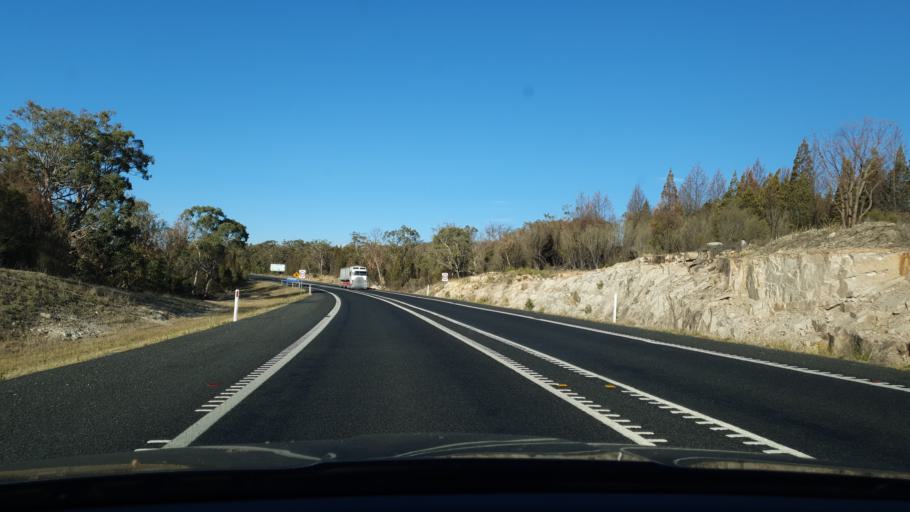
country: AU
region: Queensland
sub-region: Southern Downs
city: Stanthorpe
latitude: -28.6833
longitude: 151.9177
